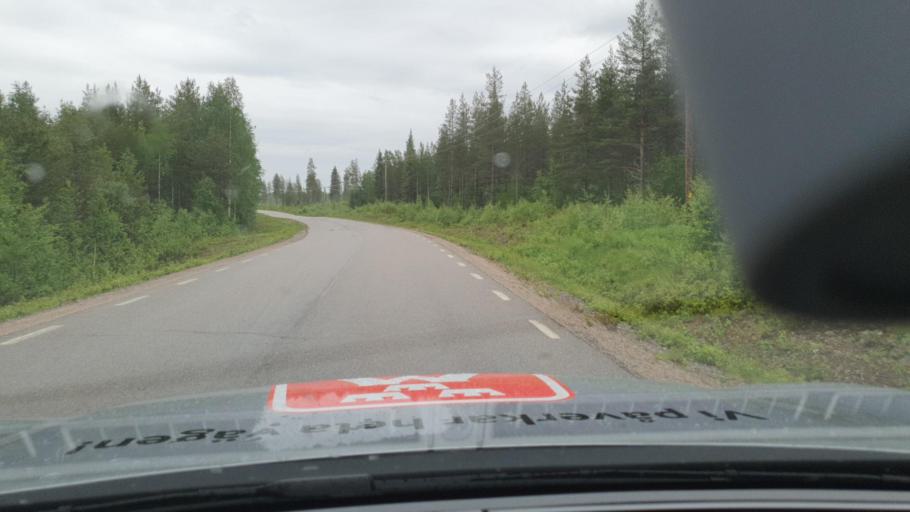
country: SE
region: Norrbotten
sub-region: Pajala Kommun
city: Pajala
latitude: 66.7628
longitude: 23.1545
